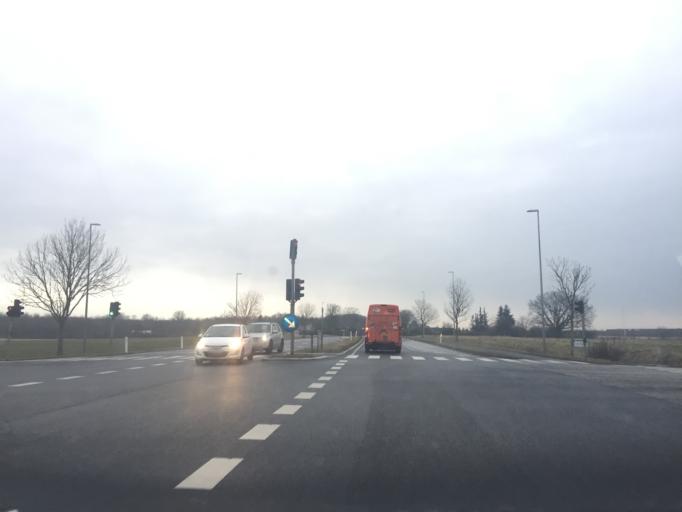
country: DK
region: Zealand
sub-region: Greve Kommune
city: Greve
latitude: 55.5894
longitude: 12.2466
